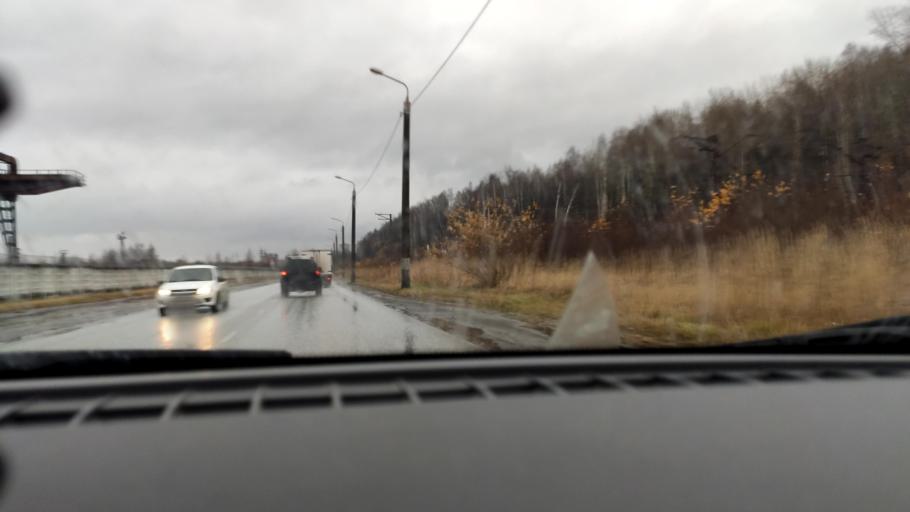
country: RU
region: Perm
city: Perm
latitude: 58.0954
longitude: 56.3558
